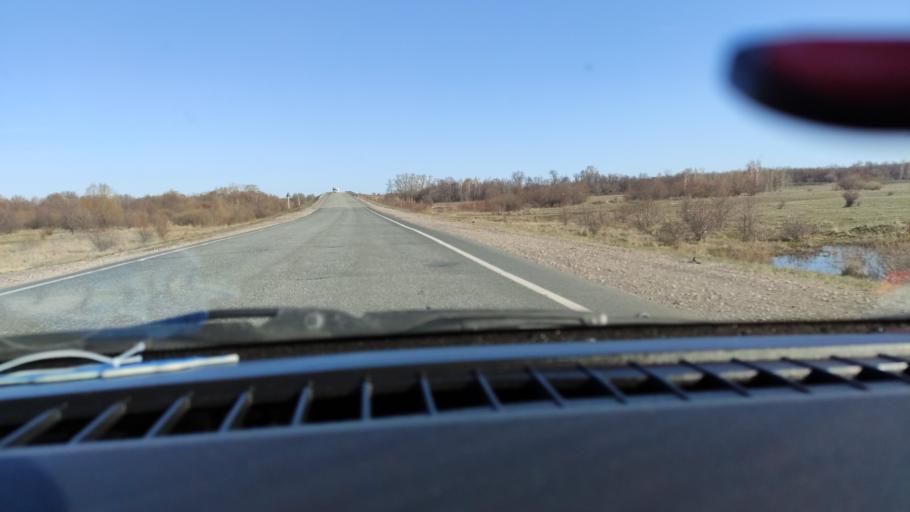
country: RU
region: Samara
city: Varlamovo
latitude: 53.1609
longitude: 48.2836
